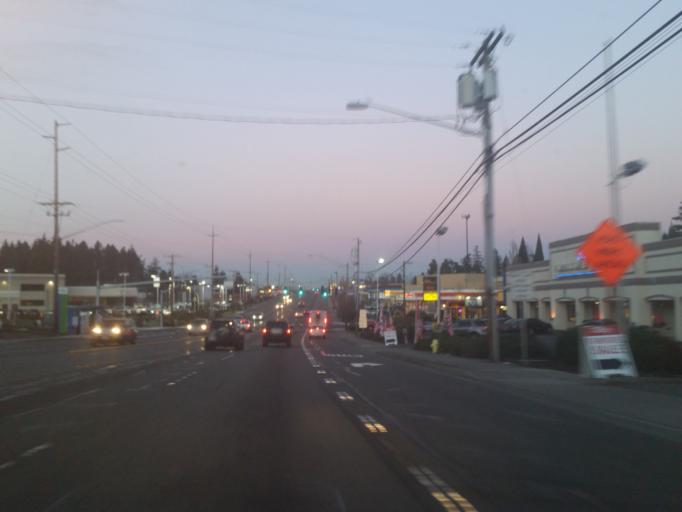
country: US
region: Washington
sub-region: Snohomish County
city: Lynnwood
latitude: 47.8131
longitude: -122.3219
